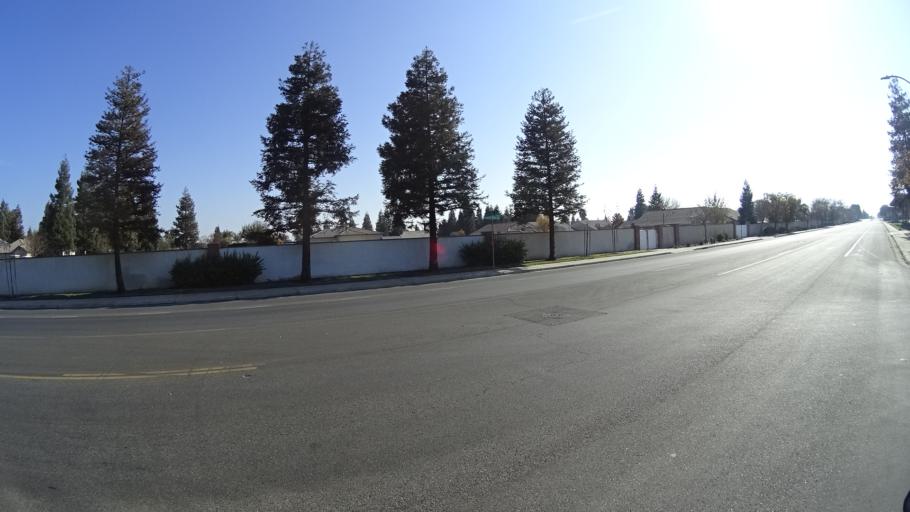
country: US
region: California
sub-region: Kern County
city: Greenacres
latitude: 35.3146
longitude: -119.1189
